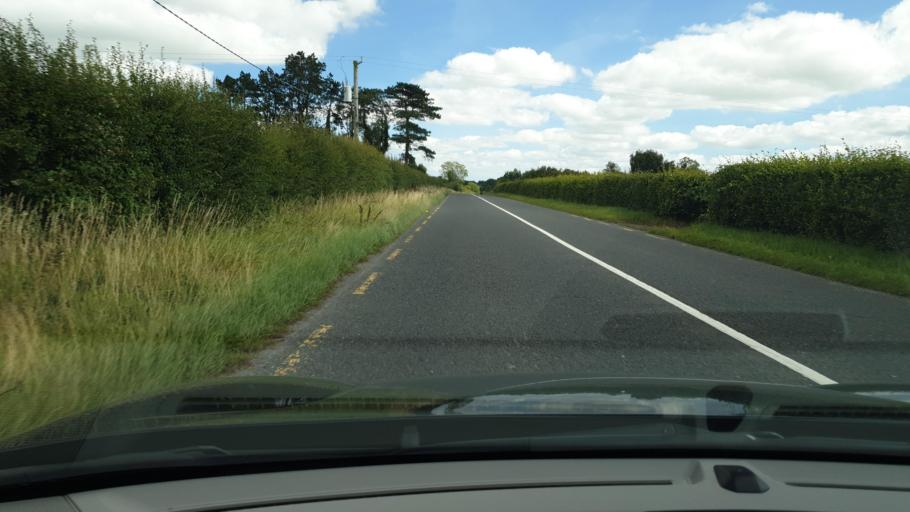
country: IE
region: Leinster
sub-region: An Mhi
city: Dunshaughlin
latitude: 53.5166
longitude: -6.6313
